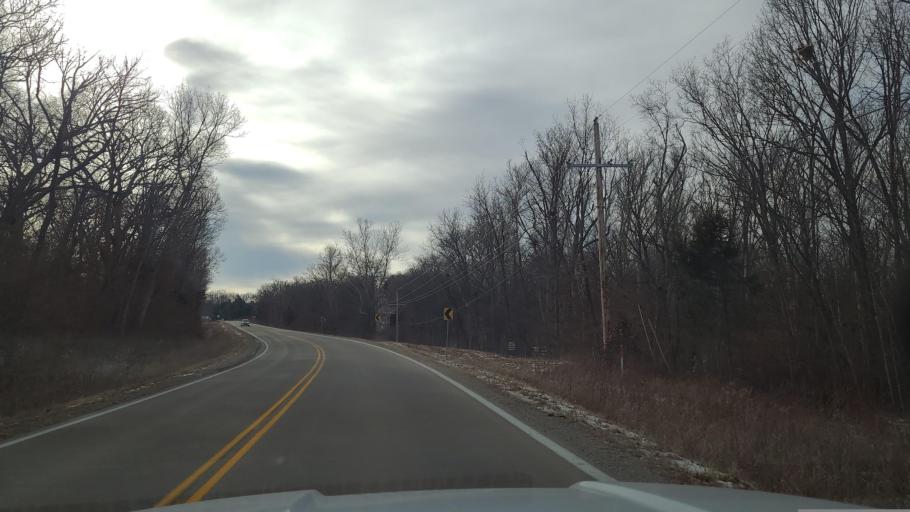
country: US
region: Kansas
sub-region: Douglas County
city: Baldwin City
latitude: 38.8105
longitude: -95.1865
